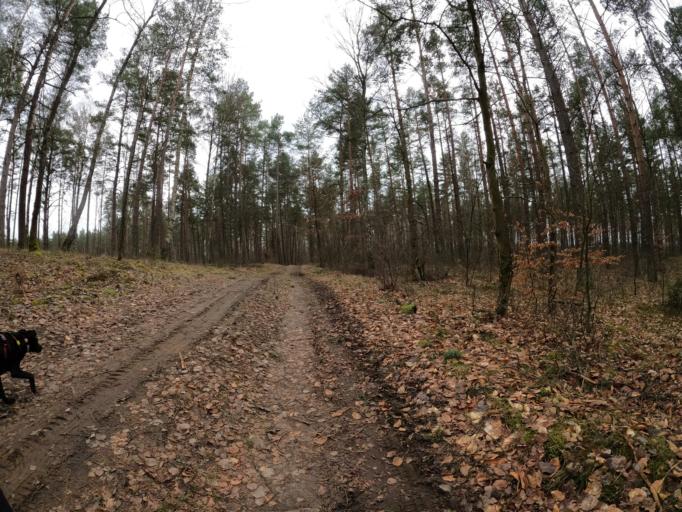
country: PL
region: Greater Poland Voivodeship
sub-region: Powiat zlotowski
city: Sypniewo
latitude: 53.4813
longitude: 16.5179
